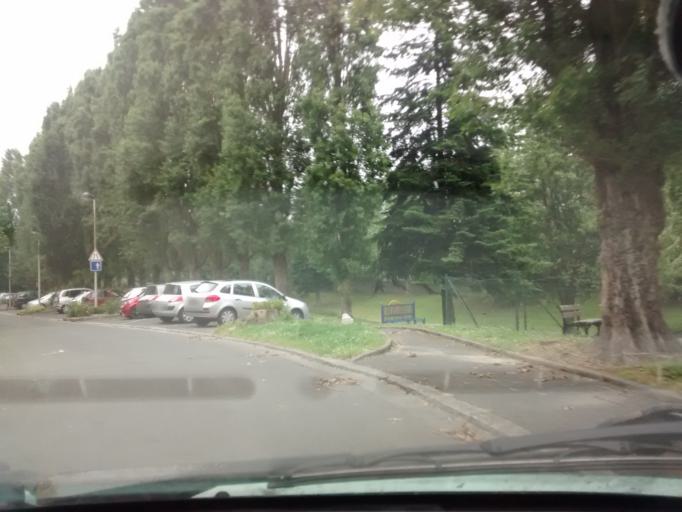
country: FR
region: Lower Normandy
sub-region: Departement de la Manche
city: Saint-Lo
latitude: 49.1086
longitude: -1.0844
